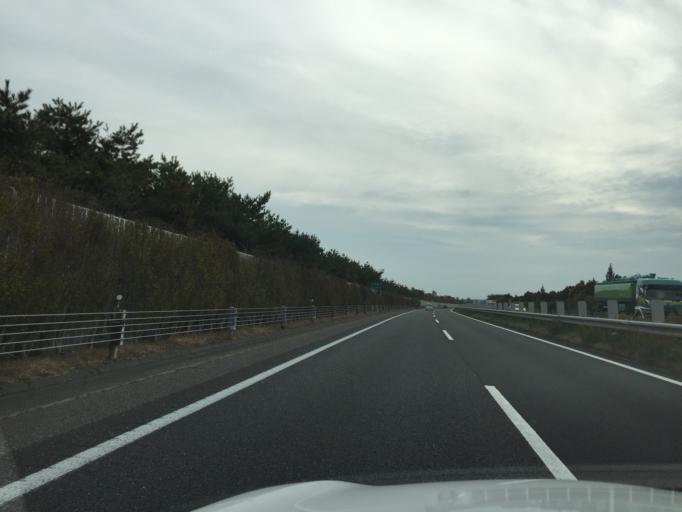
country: JP
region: Fukushima
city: Koriyama
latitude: 37.3856
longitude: 140.3125
